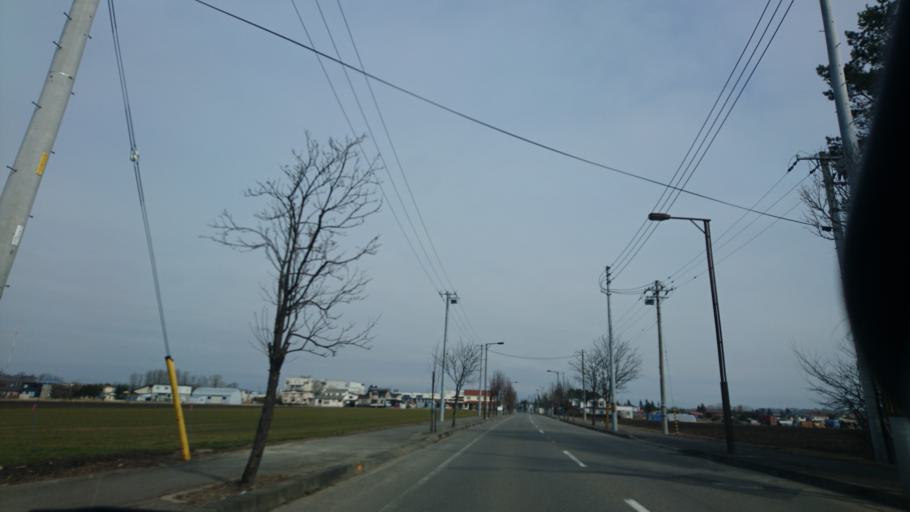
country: JP
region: Hokkaido
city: Otofuke
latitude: 42.9732
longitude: 143.2123
